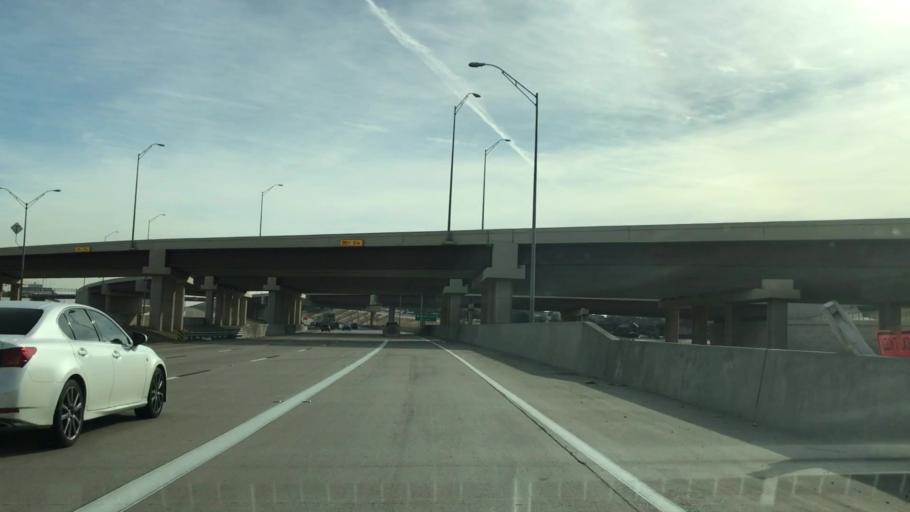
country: US
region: Texas
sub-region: Tarrant County
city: Grapevine
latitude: 32.9236
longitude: -97.0856
